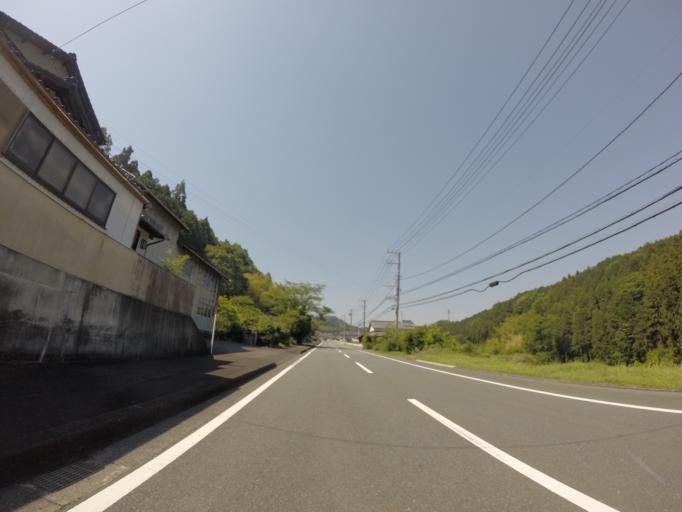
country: JP
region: Shizuoka
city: Fujinomiya
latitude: 35.2059
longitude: 138.5870
